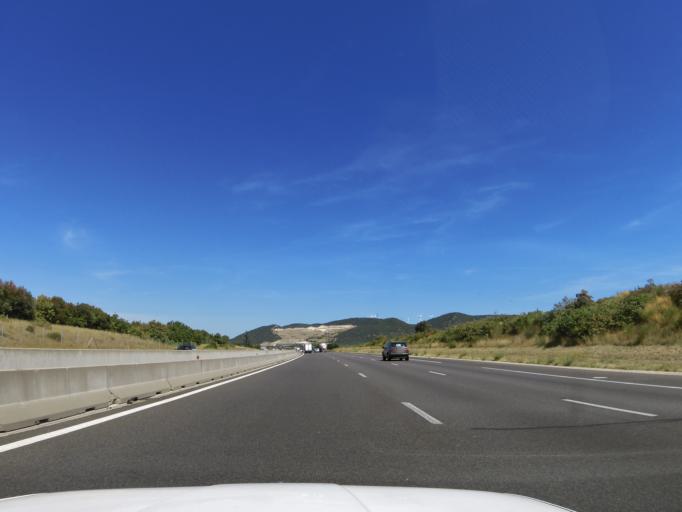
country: FR
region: Rhone-Alpes
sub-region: Departement de la Drome
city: Donzere
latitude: 44.4342
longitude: 4.7464
